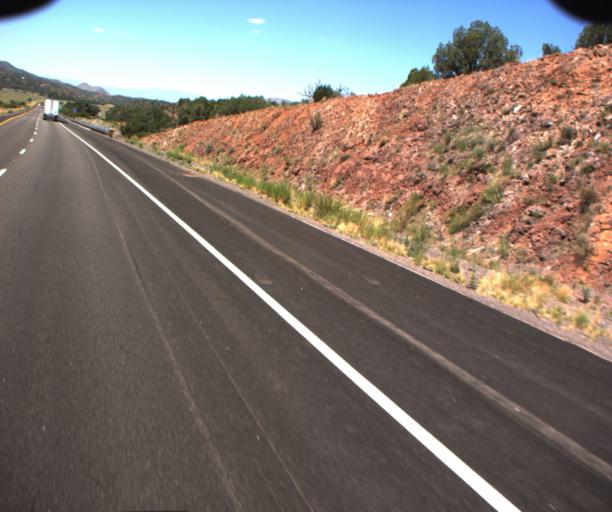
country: US
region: Arizona
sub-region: Mohave County
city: Peach Springs
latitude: 35.1901
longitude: -113.4421
